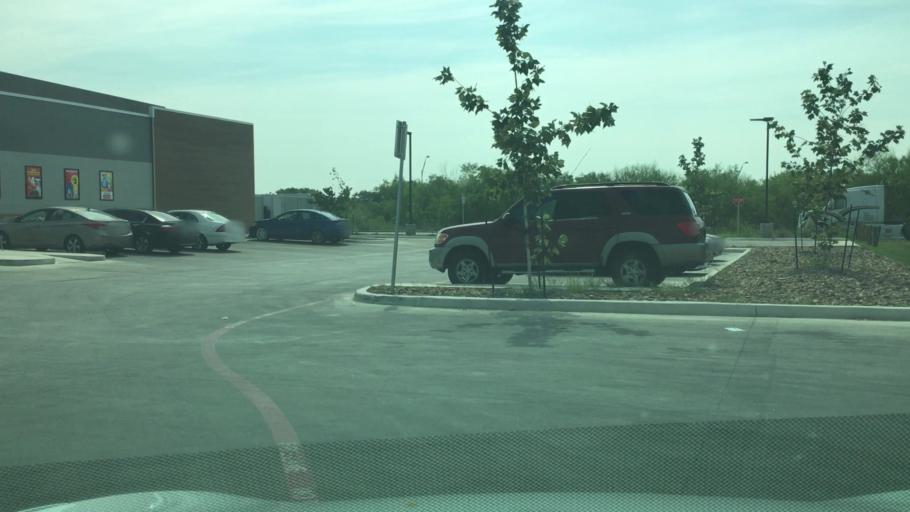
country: US
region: Texas
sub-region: Bexar County
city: Helotes
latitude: 29.5134
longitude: -98.6945
